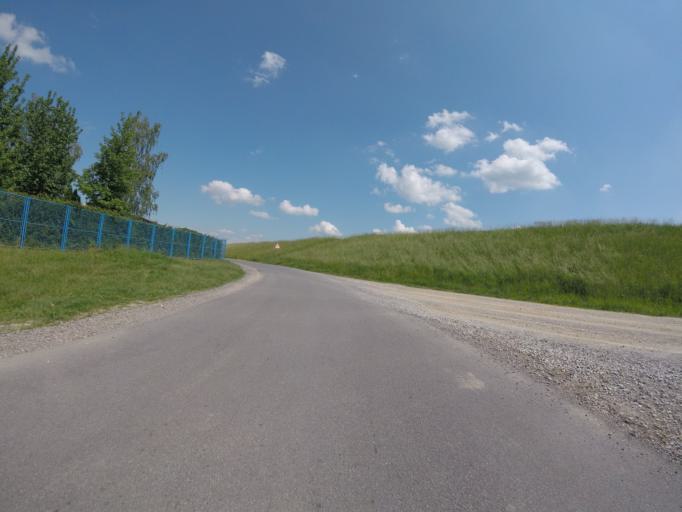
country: HR
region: Zagrebacka
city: Kuce
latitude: 45.6694
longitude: 16.1752
